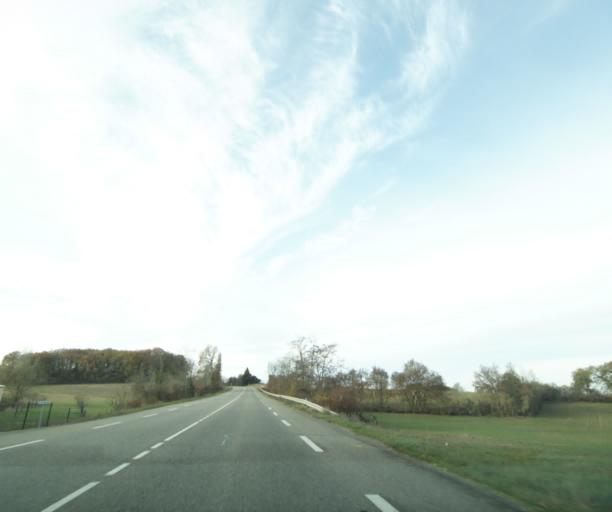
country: FR
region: Midi-Pyrenees
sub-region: Departement du Gers
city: Jegun
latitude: 43.7193
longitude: 0.4163
